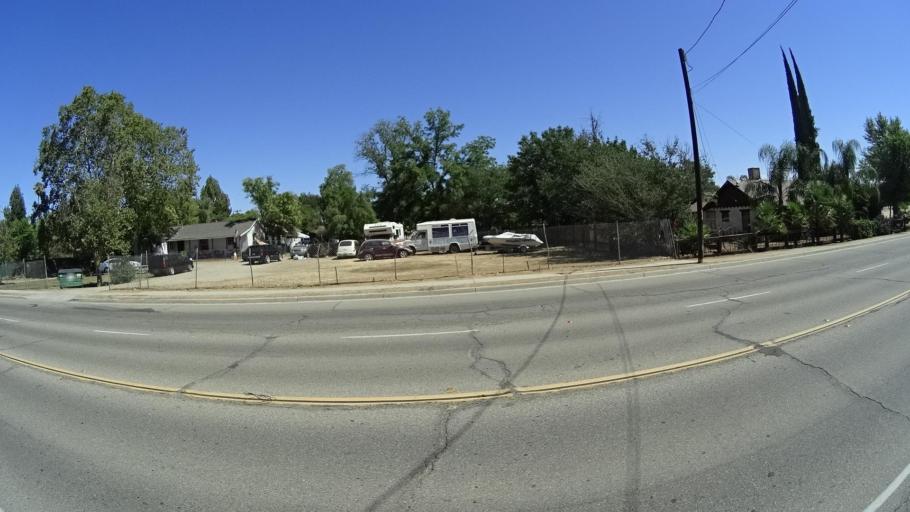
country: US
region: California
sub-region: Fresno County
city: Sunnyside
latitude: 36.7431
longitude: -119.7122
